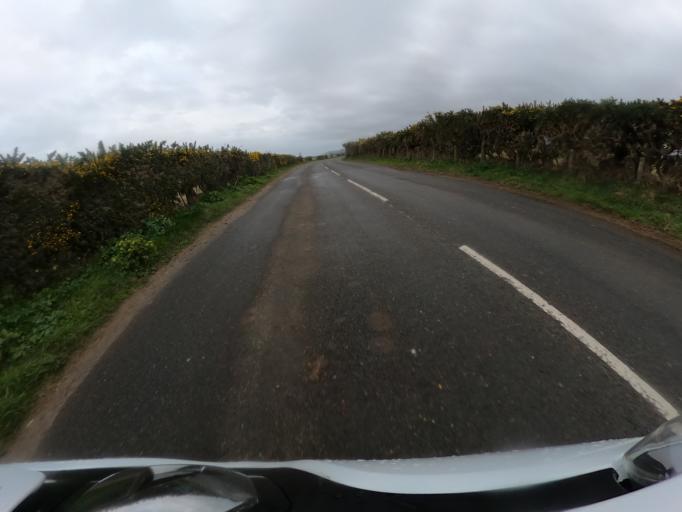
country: IM
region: Ramsey
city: Ramsey
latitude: 54.3573
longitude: -4.5139
